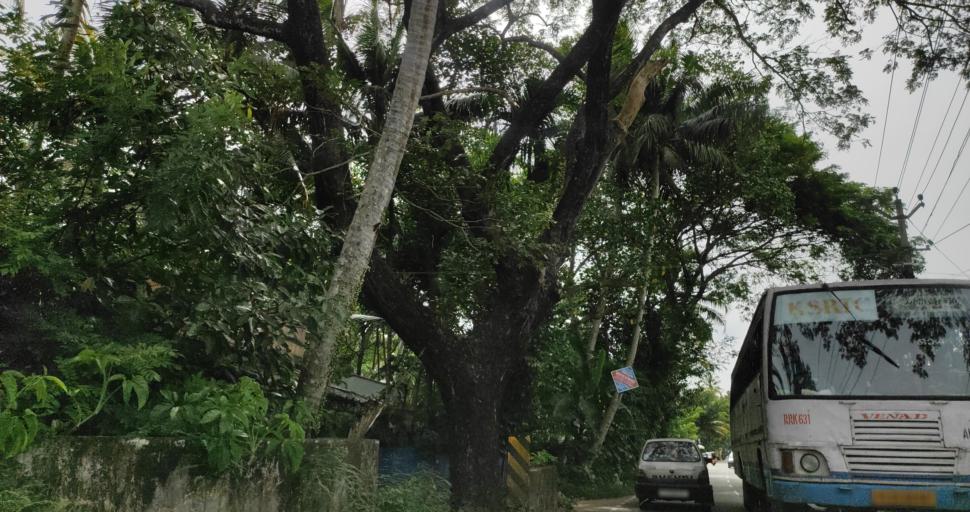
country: IN
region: Kerala
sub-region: Alappuzha
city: Shertallai
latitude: 9.6836
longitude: 76.3550
